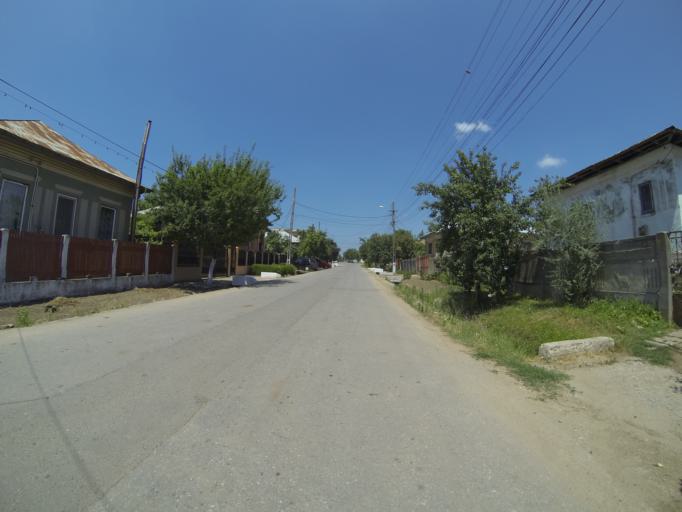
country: RO
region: Dolj
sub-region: Comuna Segarcea
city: Segarcea
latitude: 44.0924
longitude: 23.7463
